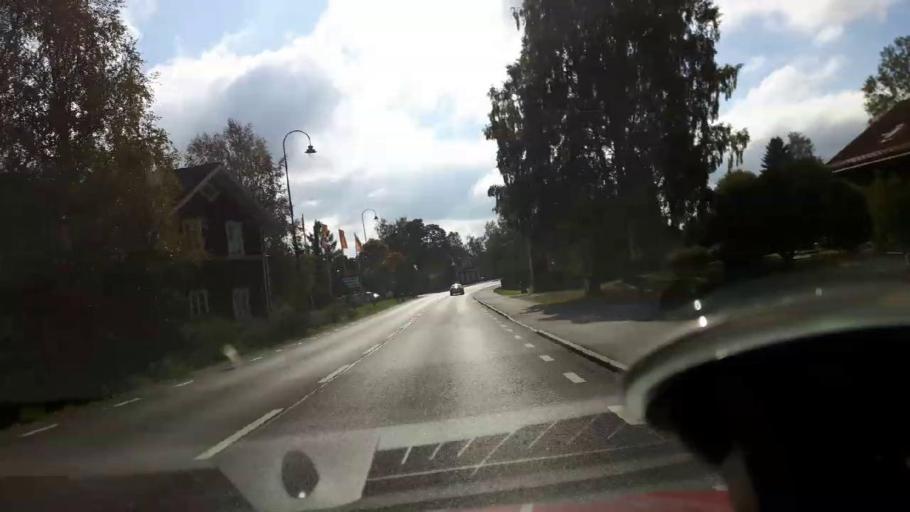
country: SE
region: Gaevleborg
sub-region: Ljusdals Kommun
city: Jaervsoe
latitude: 61.7195
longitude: 16.1694
